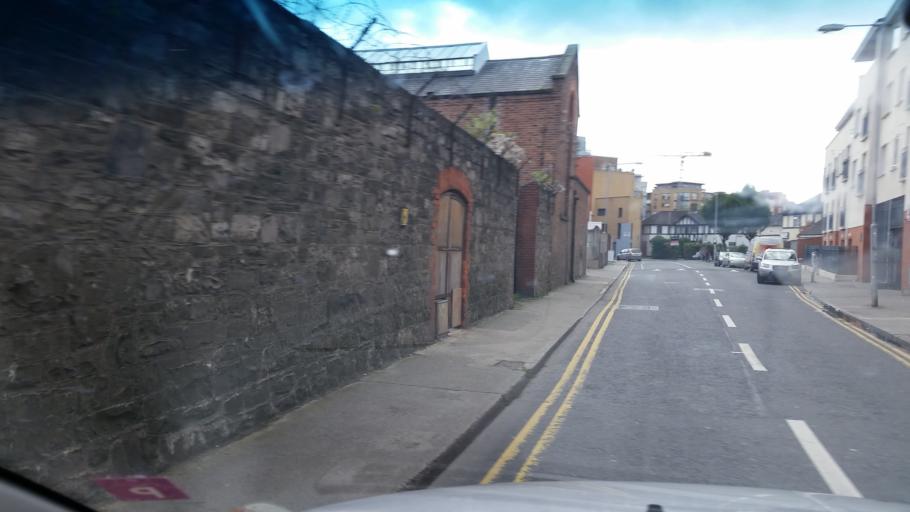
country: IE
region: Leinster
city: Rialto
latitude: 53.3387
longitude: -6.2869
